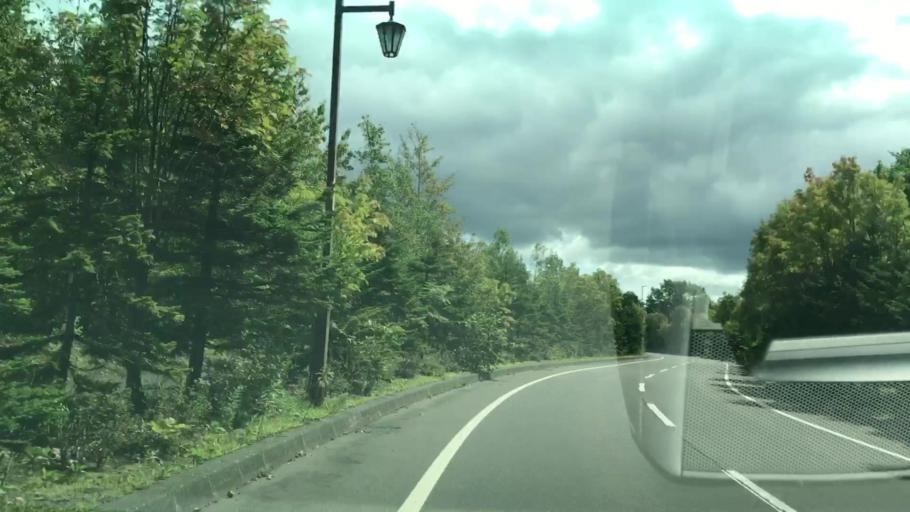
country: JP
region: Hokkaido
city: Chitose
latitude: 42.7788
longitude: 141.6034
